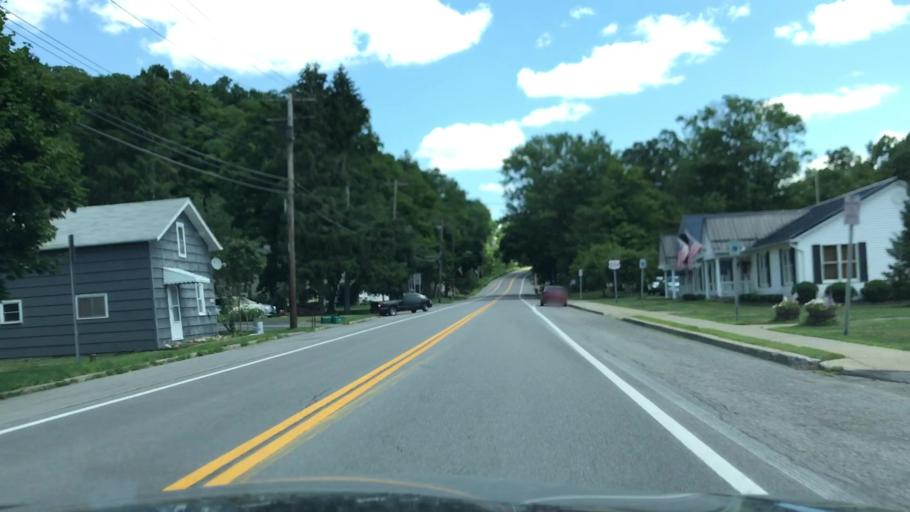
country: US
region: New York
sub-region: Erie County
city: East Aurora
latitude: 42.7681
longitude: -78.5280
